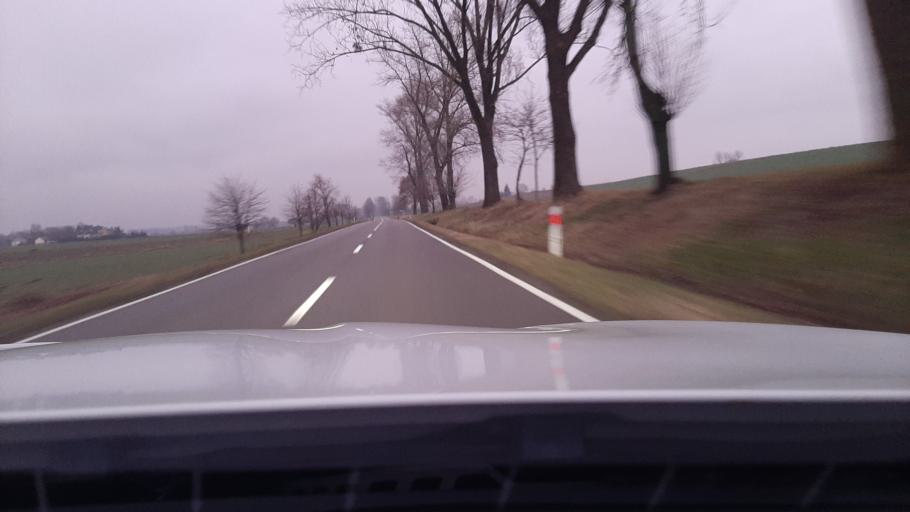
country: PL
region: Lublin Voivodeship
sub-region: Powiat lubelski
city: Garbow
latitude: 51.3471
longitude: 22.3768
